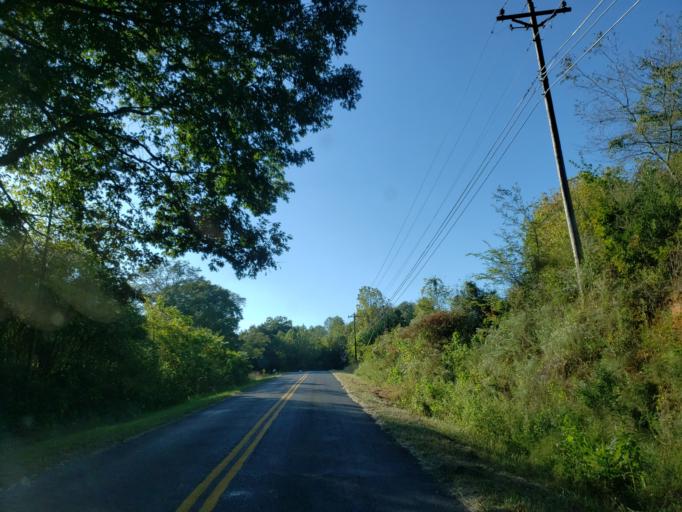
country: US
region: Georgia
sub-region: Pickens County
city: Nelson
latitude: 34.3888
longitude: -84.4100
